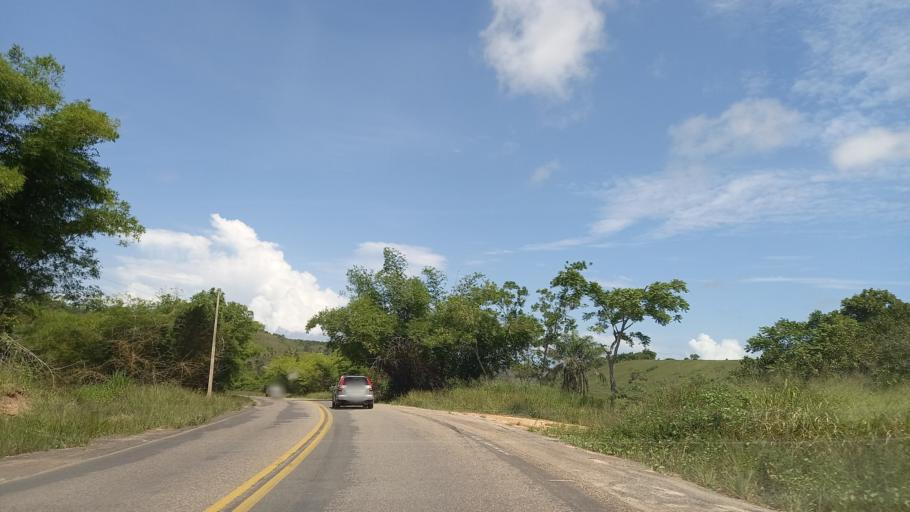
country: BR
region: Pernambuco
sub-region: Barreiros
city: Barreiros
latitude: -8.8576
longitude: -35.1675
